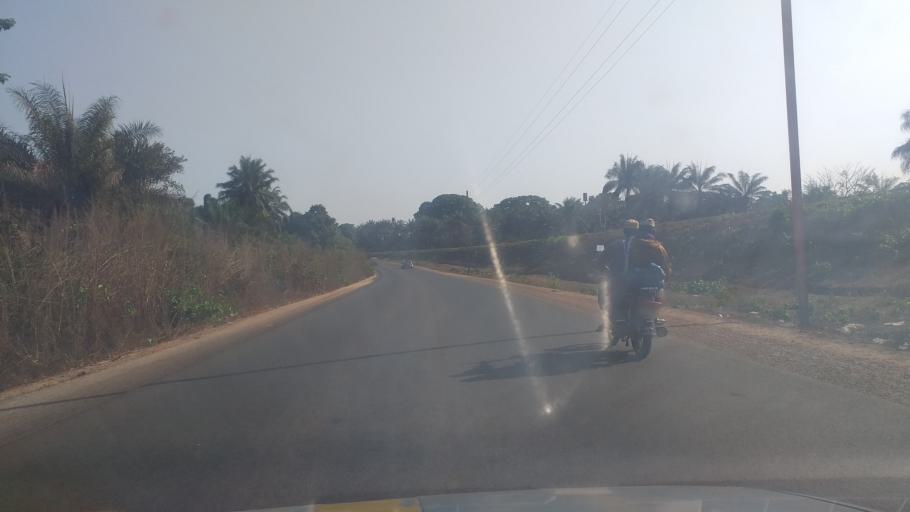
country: GN
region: Boke
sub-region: Boke Prefecture
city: Kamsar
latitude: 10.7107
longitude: -14.5246
